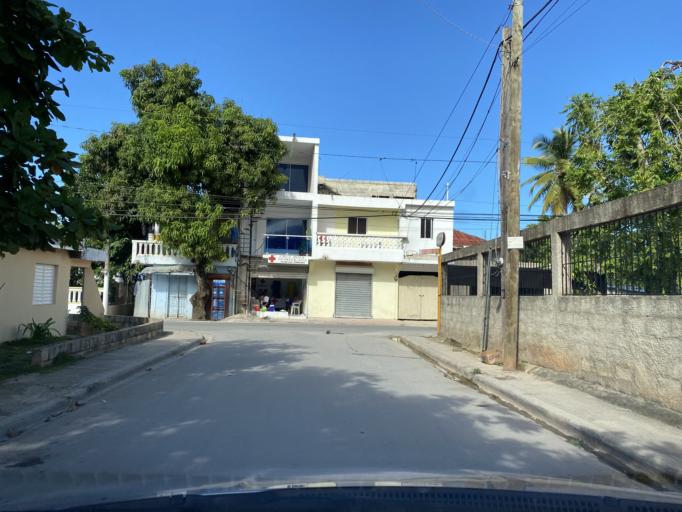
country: DO
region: Samana
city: Las Terrenas
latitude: 19.3085
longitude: -69.5428
